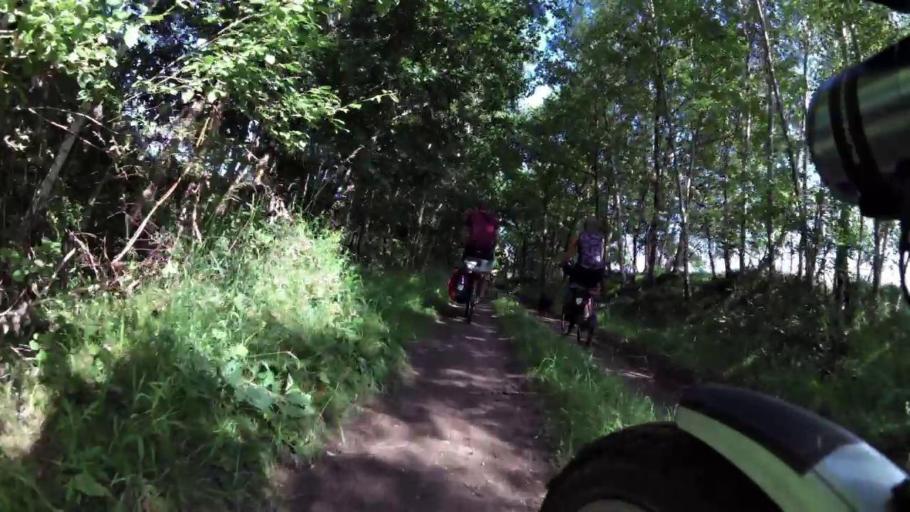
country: PL
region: West Pomeranian Voivodeship
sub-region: Powiat lobeski
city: Radowo Male
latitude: 53.5839
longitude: 15.4473
